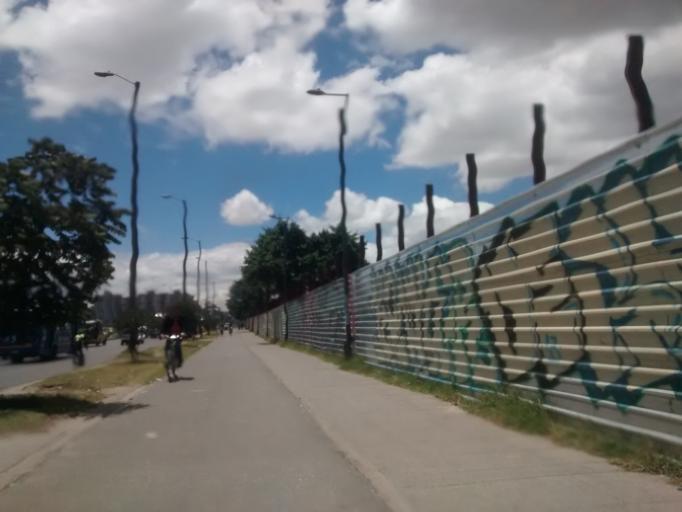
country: CO
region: Bogota D.C.
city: Bogota
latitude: 4.6468
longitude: -74.1496
